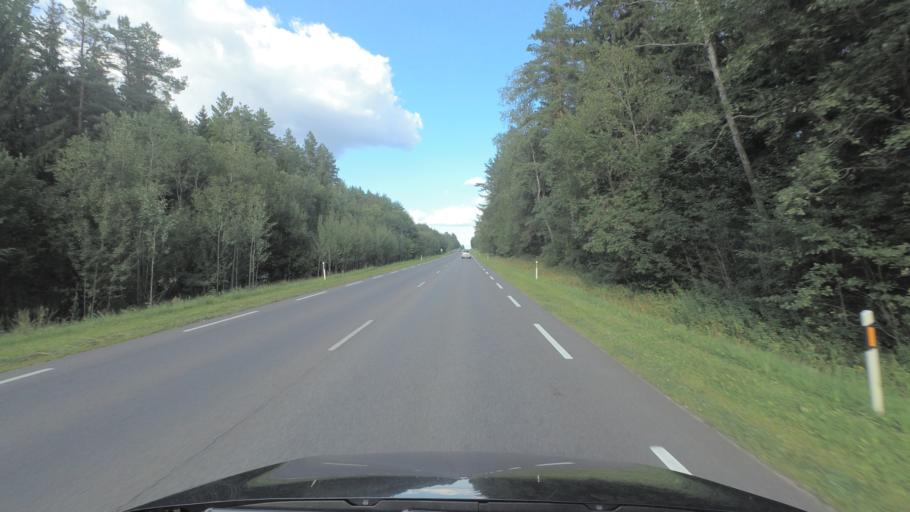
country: LT
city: Pabrade
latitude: 54.9717
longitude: 25.7320
